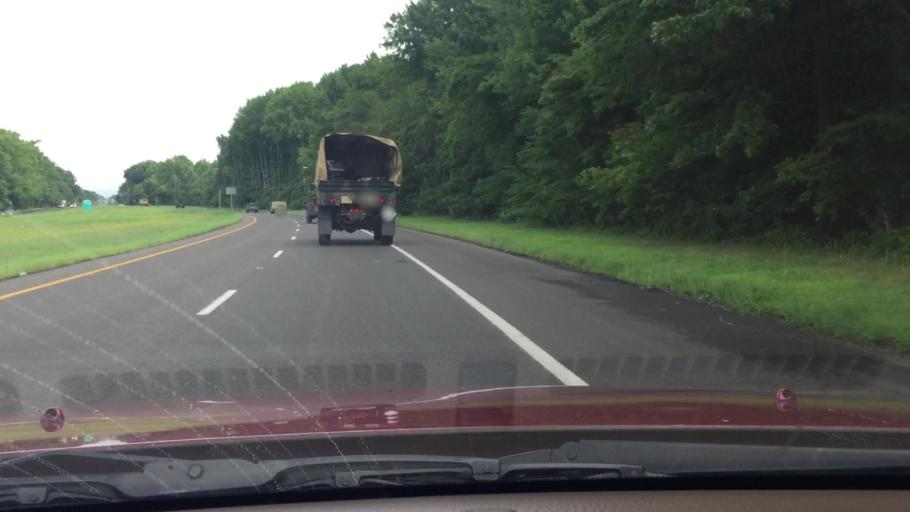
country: US
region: New Jersey
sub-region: Burlington County
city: Fort Dix
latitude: 40.0712
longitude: -74.6558
